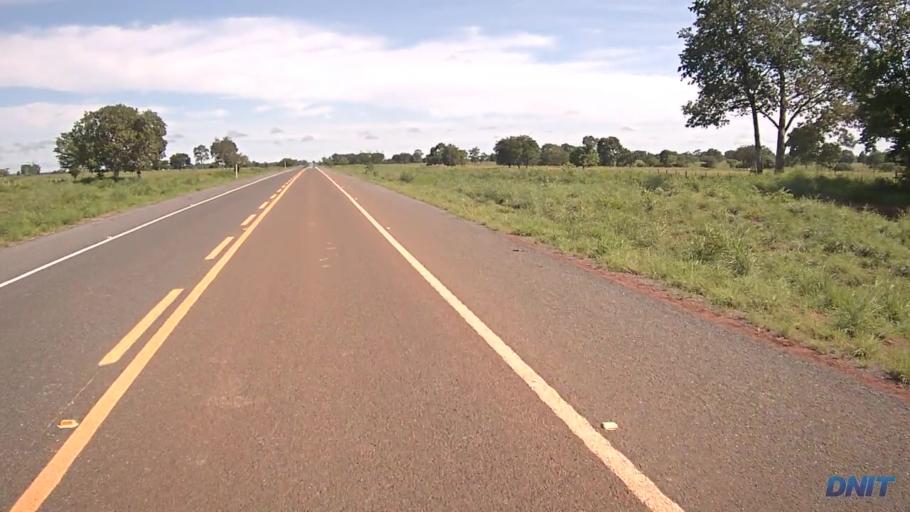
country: BR
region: Goias
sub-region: Sao Miguel Do Araguaia
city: Sao Miguel do Araguaia
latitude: -13.4692
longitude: -50.1153
